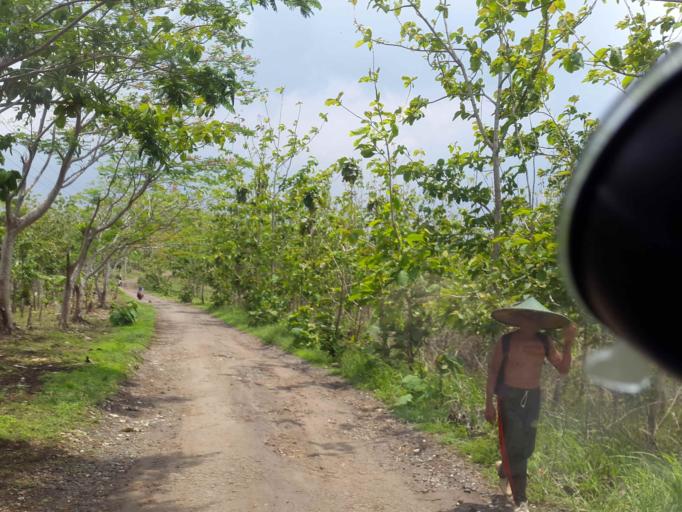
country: ID
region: East Java
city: Tumpakoyot
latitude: -8.2914
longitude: 112.0285
